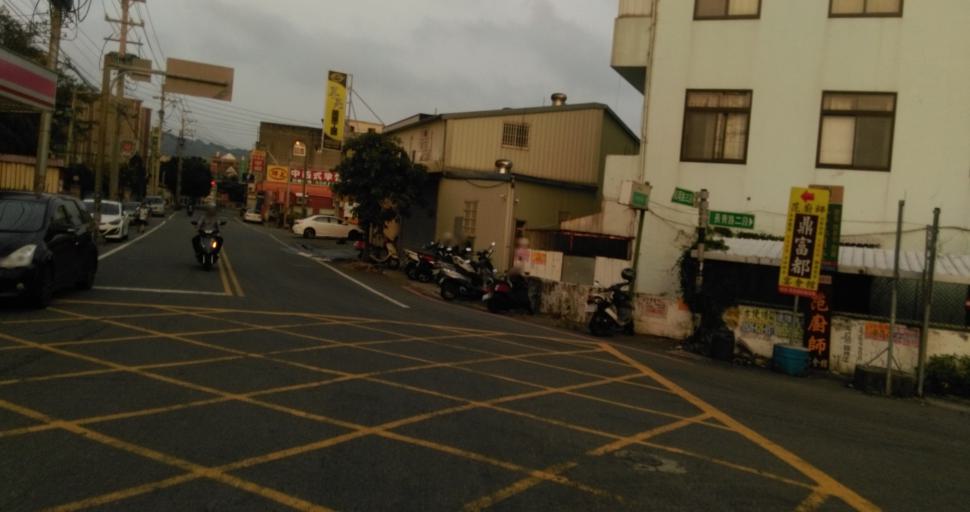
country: TW
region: Taiwan
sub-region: Hsinchu
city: Zhubei
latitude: 24.8606
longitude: 120.9630
